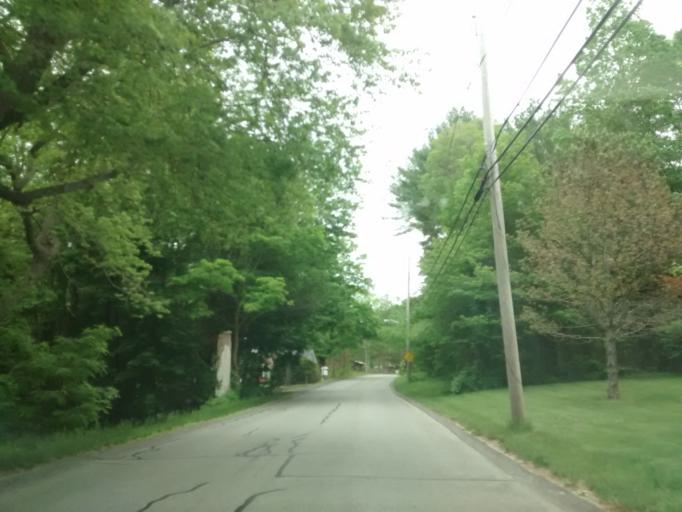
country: US
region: Rhode Island
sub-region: Providence County
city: Harrisville
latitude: 41.9620
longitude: -71.6657
